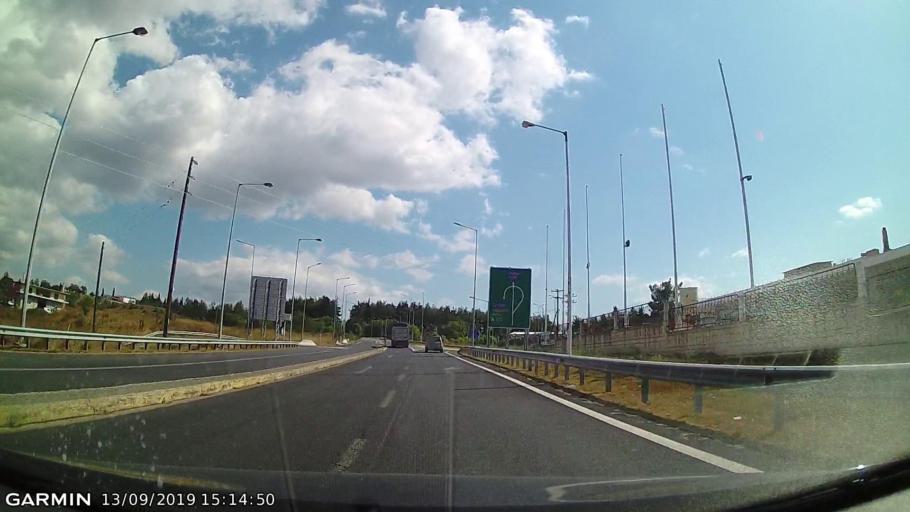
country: GR
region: Peloponnese
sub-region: Nomos Arkadias
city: Tripoli
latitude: 37.4921
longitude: 22.3794
